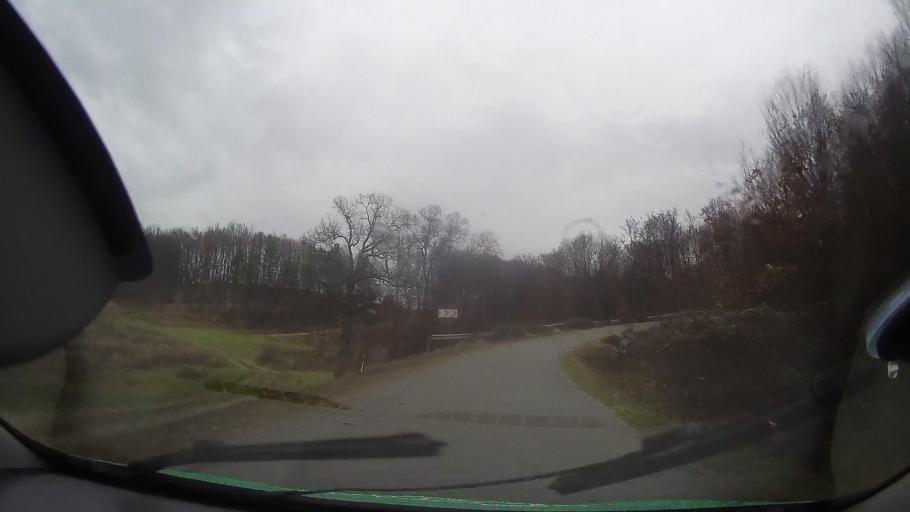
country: RO
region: Bihor
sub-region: Comuna Rabagani
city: Rabagani
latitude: 46.7231
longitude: 22.2333
